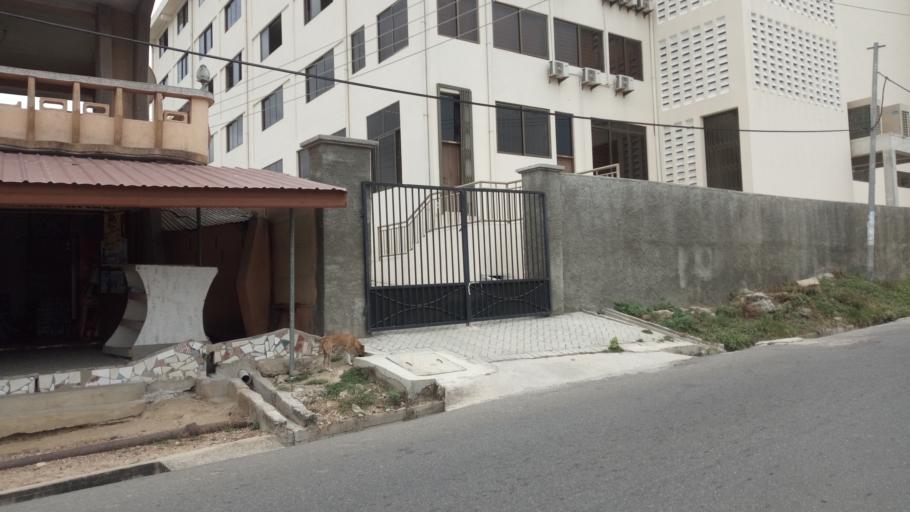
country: GH
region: Central
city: Winneba
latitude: 5.3453
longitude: -0.6264
